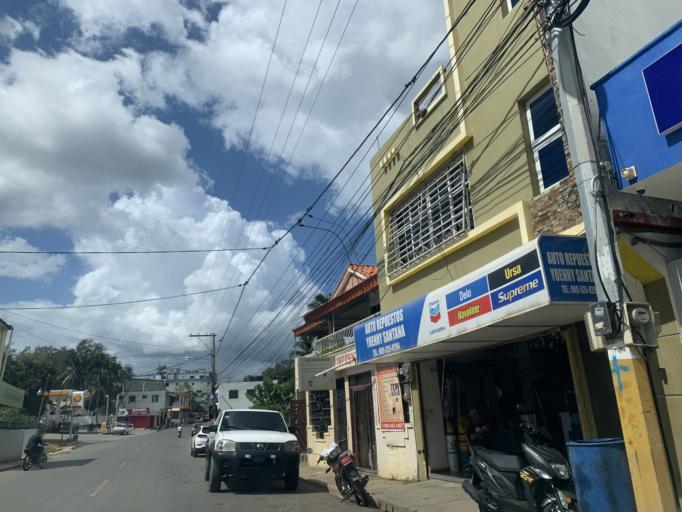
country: DO
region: Monte Plata
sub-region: Yamasa
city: Yamasa
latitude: 18.7657
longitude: -70.0214
